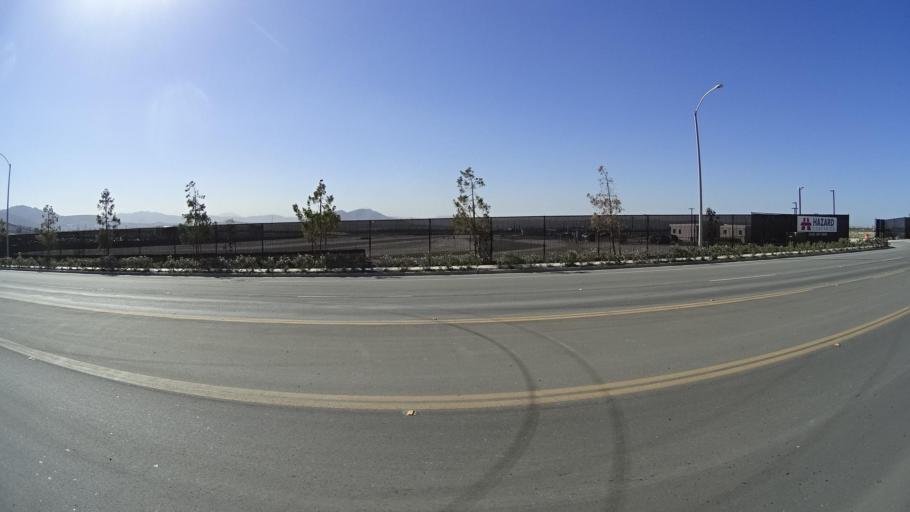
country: MX
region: Baja California
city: Tijuana
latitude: 32.5674
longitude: -116.9151
